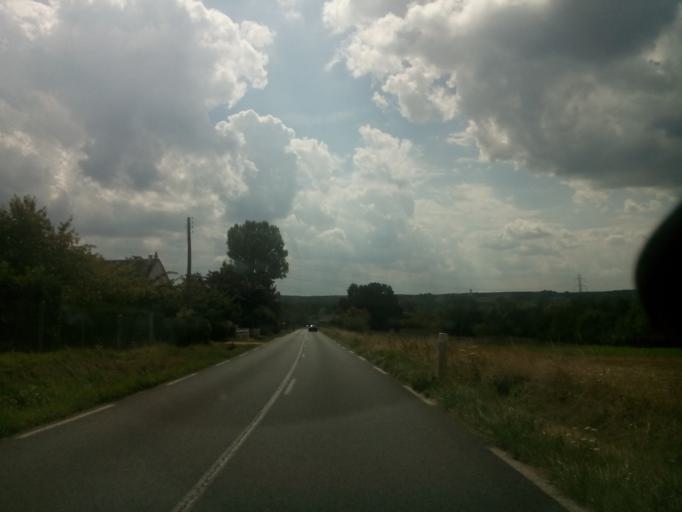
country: FR
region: Centre
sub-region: Departement d'Indre-et-Loire
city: Cheille
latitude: 47.2766
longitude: 0.4244
